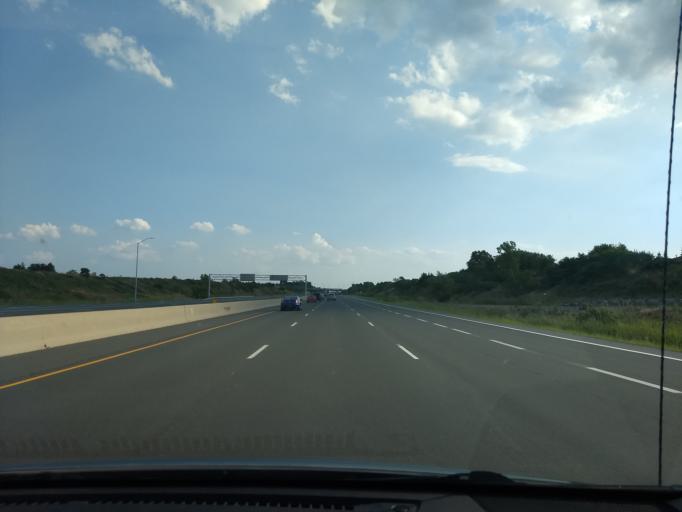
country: CA
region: Ontario
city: Burlington
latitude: 43.3809
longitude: -79.8333
